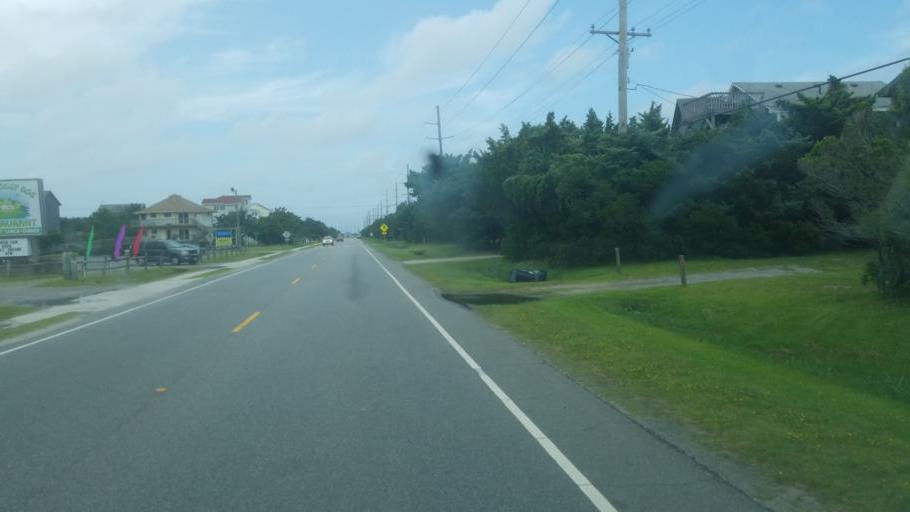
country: US
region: North Carolina
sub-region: Dare County
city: Buxton
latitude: 35.3601
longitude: -75.5013
